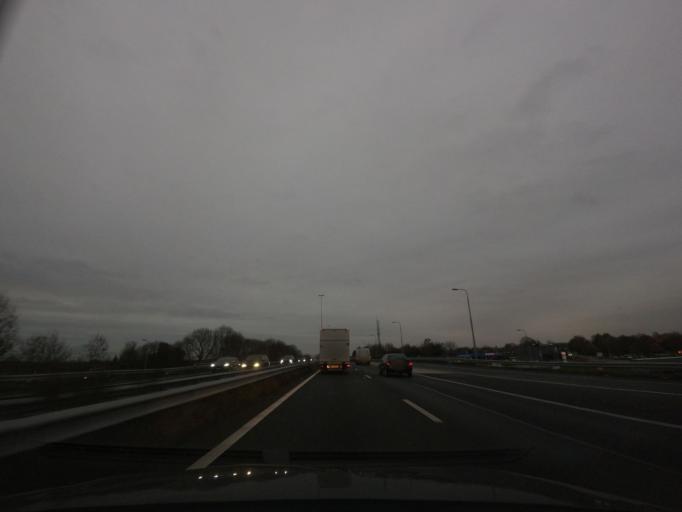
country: NL
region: North Brabant
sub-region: Gemeente Woudrichem
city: Almkerk
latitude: 51.7725
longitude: 4.9277
